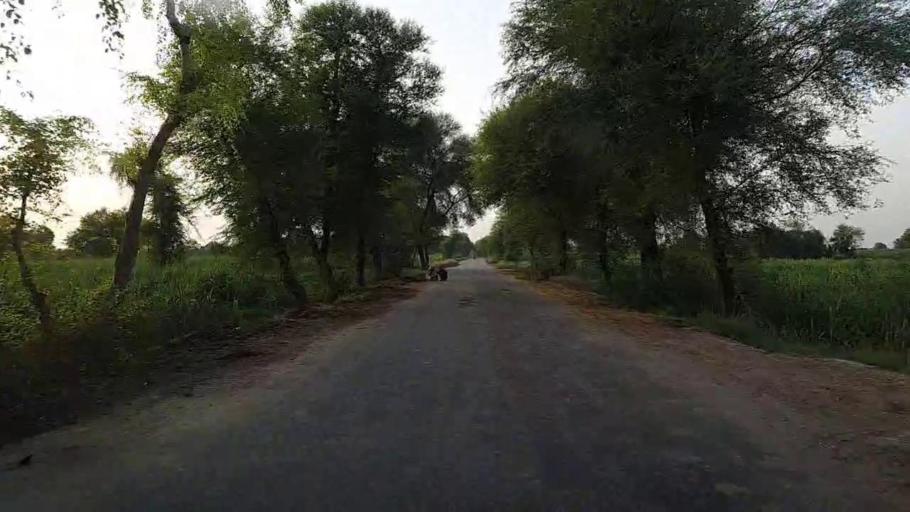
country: PK
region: Sindh
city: Ubauro
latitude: 28.2350
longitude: 69.8143
